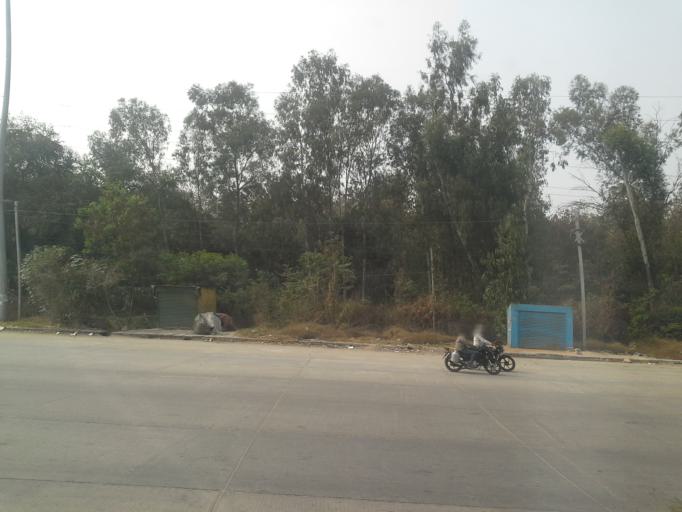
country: IN
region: Telangana
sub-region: Medak
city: Patancheru
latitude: 17.5241
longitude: 78.2727
